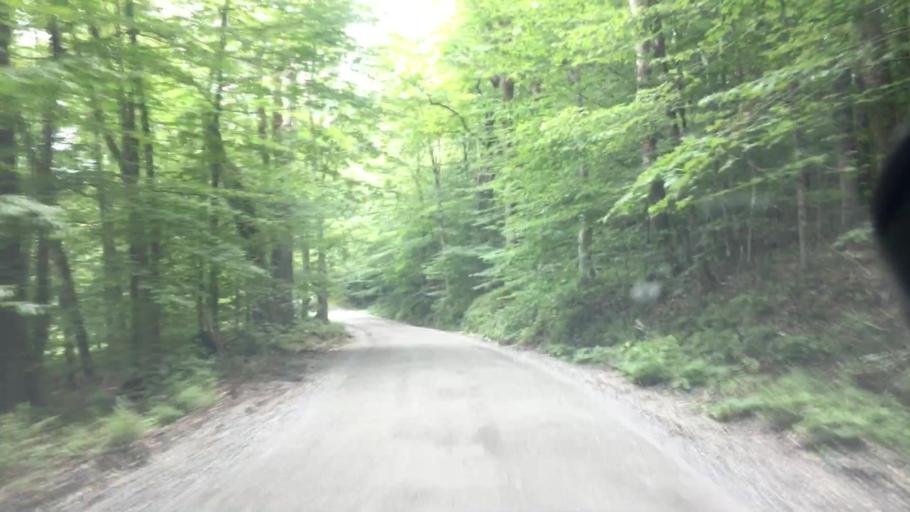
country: US
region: Vermont
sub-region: Windham County
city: Dover
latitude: 42.8468
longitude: -72.7715
